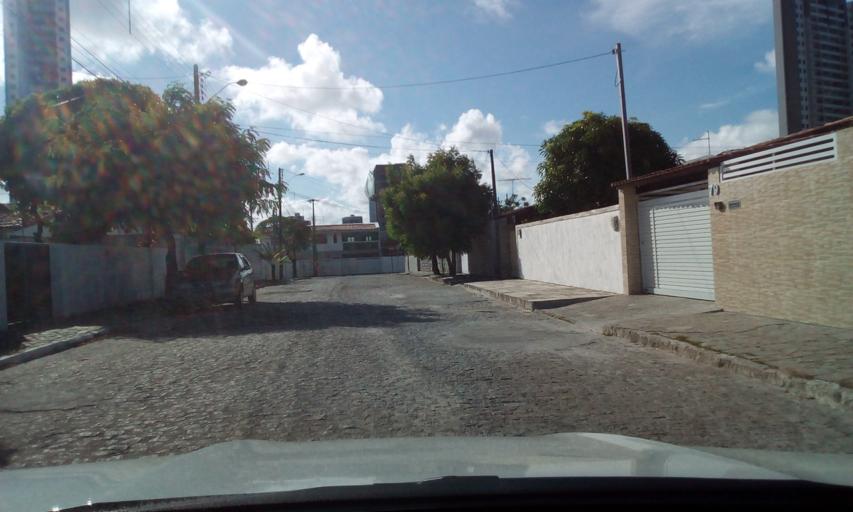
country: BR
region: Paraiba
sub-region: Joao Pessoa
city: Joao Pessoa
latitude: -7.1122
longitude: -34.8388
